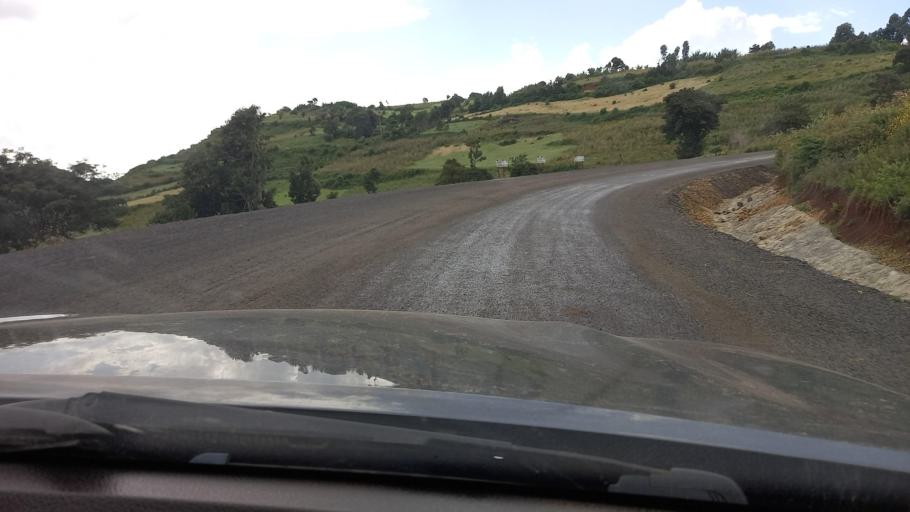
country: ET
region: Southern Nations, Nationalities, and People's Region
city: Mizan Teferi
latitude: 6.2148
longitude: 35.6371
